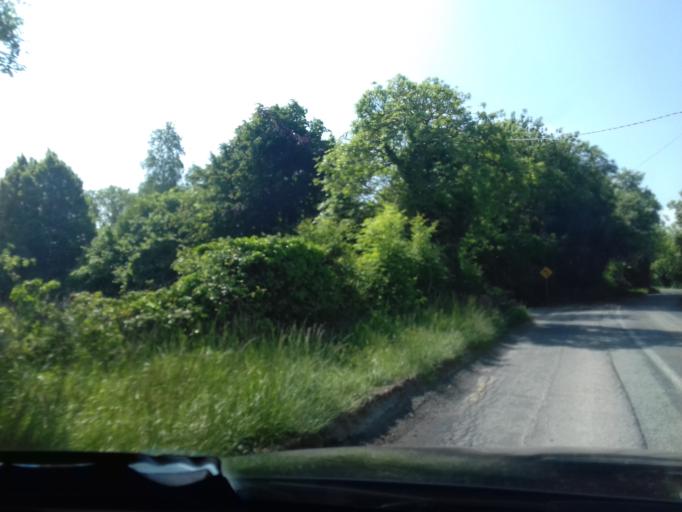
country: IE
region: Leinster
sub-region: Fingal County
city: Swords
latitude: 53.5128
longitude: -6.2268
